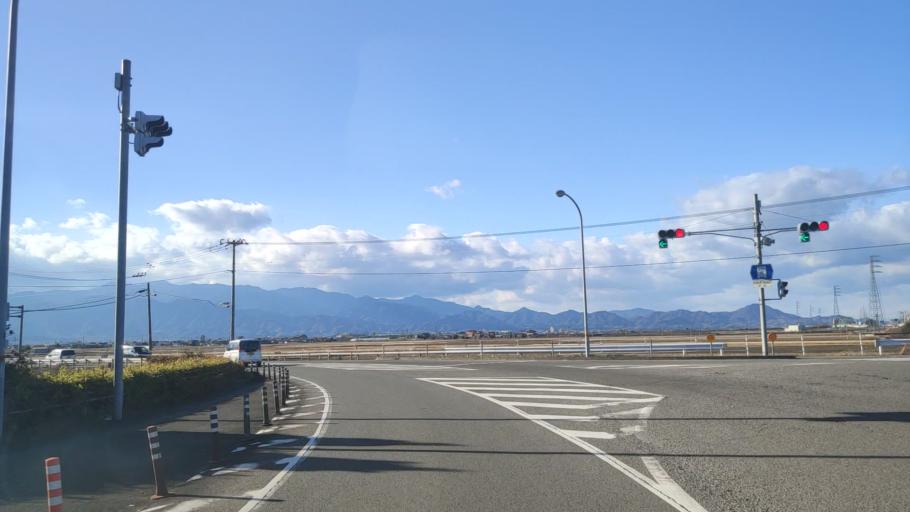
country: JP
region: Ehime
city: Saijo
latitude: 33.9189
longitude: 133.1248
